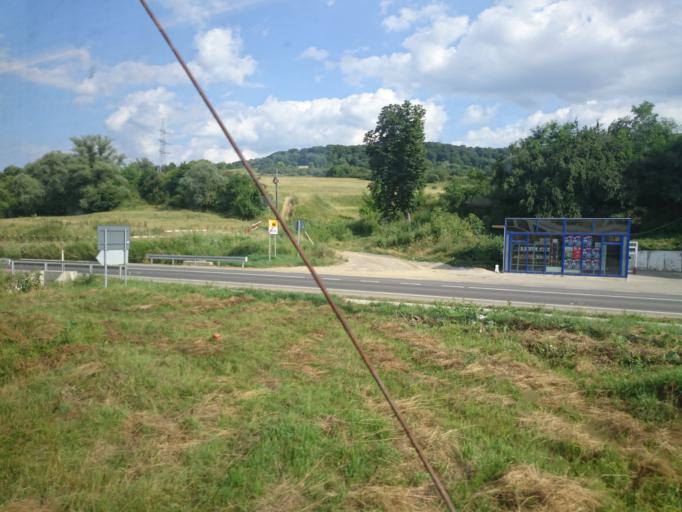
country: RO
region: Sibiu
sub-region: Oras Dumbraveni
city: Dumbraveni
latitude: 46.2163
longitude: 24.5690
